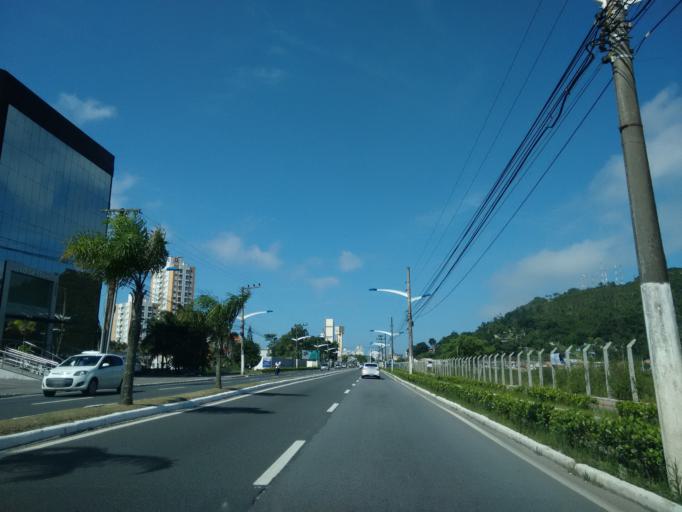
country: BR
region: Santa Catarina
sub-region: Itajai
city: Itajai
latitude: -26.9223
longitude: -48.6744
